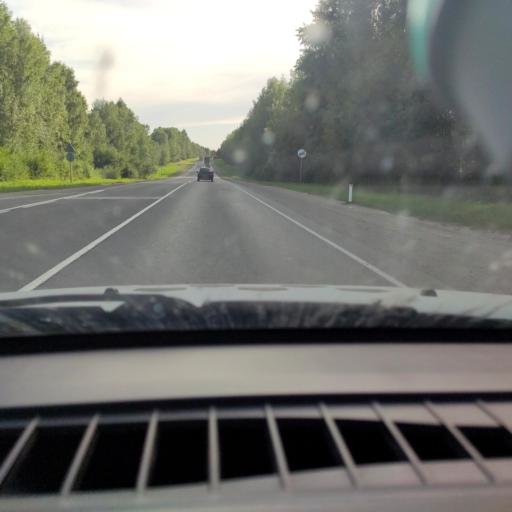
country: RU
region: Kirov
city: Vakhrushi
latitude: 58.6463
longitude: 49.8601
